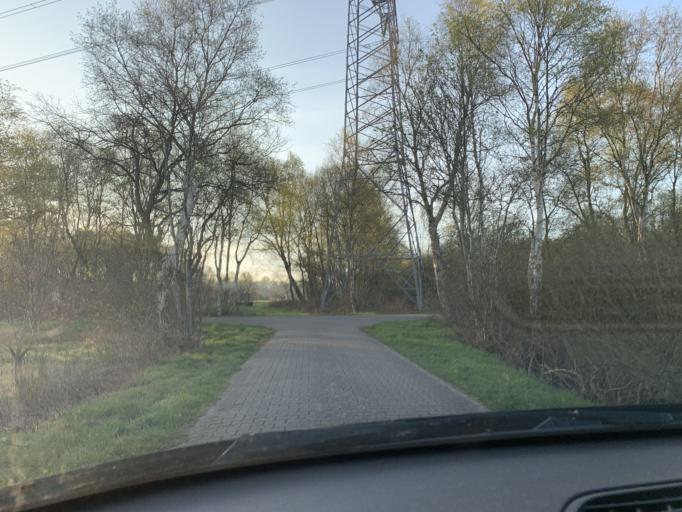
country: DE
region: Lower Saxony
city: Apen
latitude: 53.2860
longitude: 7.8267
